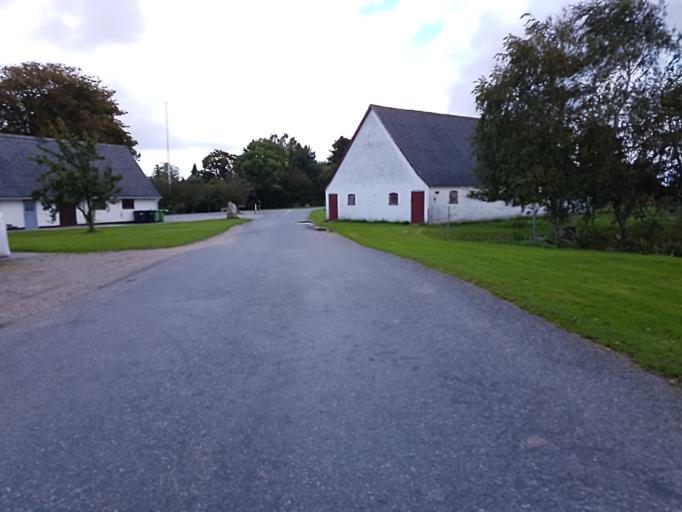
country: DK
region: Zealand
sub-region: Roskilde Kommune
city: Gundsomagle
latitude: 55.7199
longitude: 12.1585
